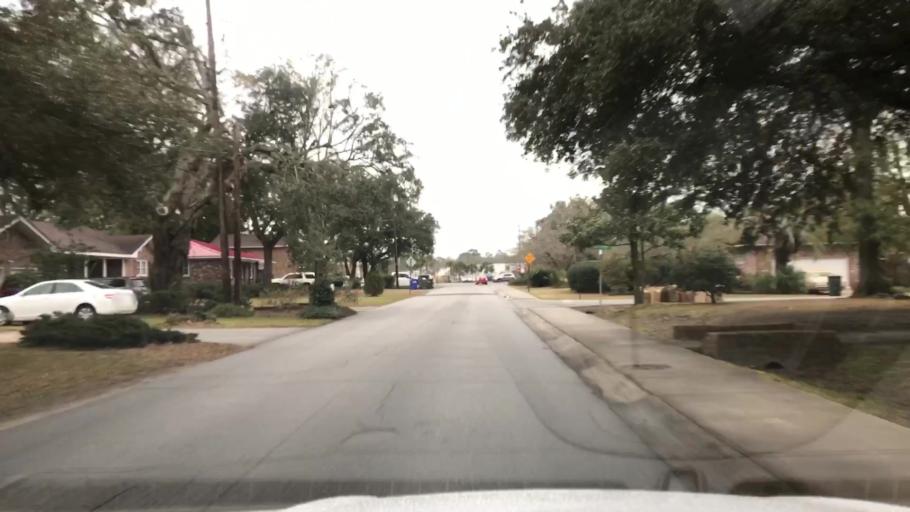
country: US
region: South Carolina
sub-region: Charleston County
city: North Charleston
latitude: 32.8158
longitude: -79.9983
